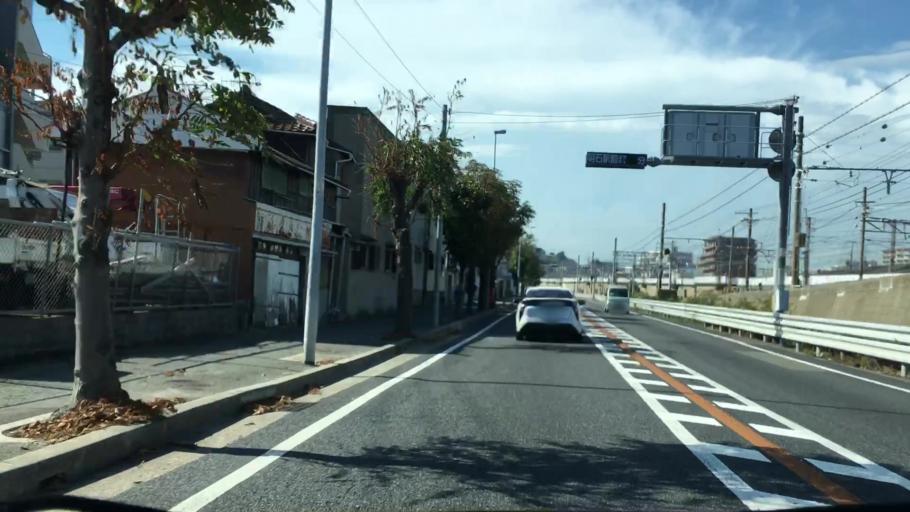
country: JP
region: Hyogo
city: Akashi
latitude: 34.6357
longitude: 135.0308
